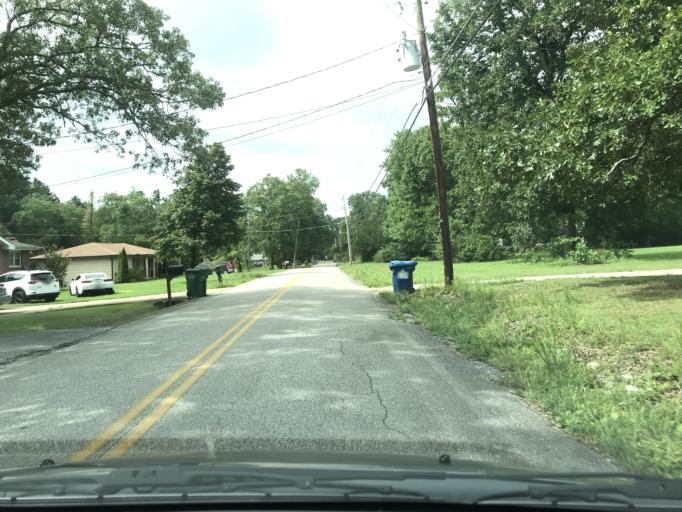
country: US
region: Tennessee
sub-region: Hamilton County
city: Lakesite
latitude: 35.1772
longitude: -85.0786
